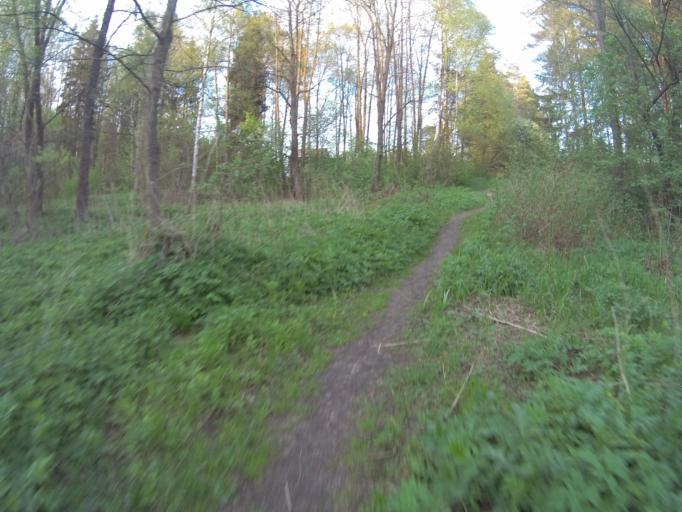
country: RU
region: Vladimir
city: Kommunar
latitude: 56.0676
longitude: 40.4761
